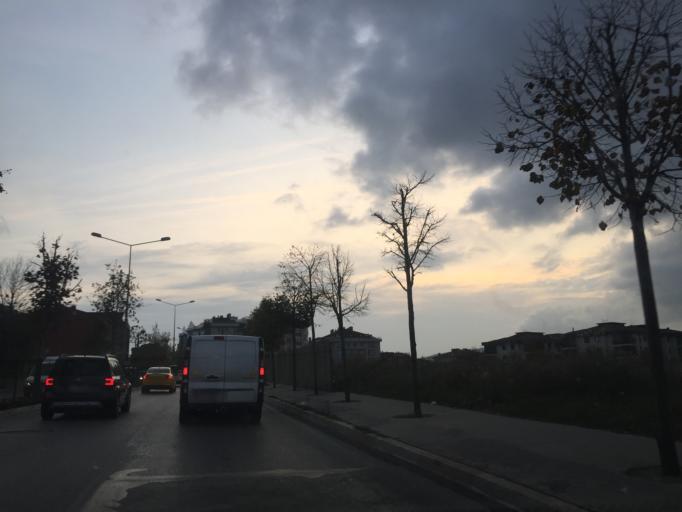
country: TR
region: Istanbul
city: Samandira
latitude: 40.9861
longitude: 29.2236
